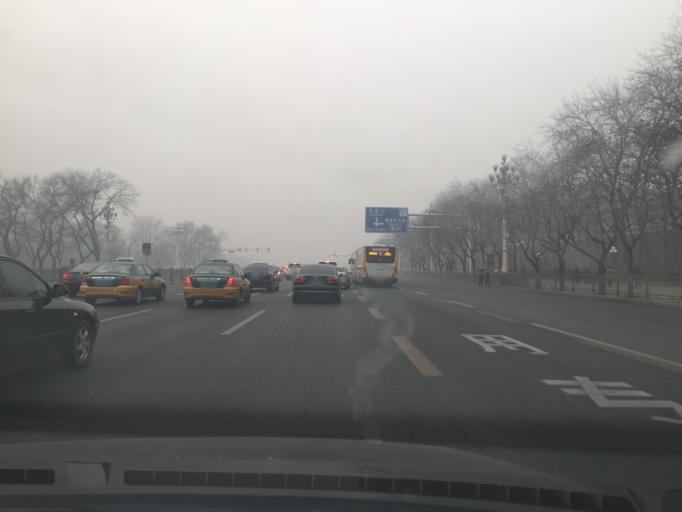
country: CN
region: Beijing
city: Beijing
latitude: 39.9066
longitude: 116.3997
